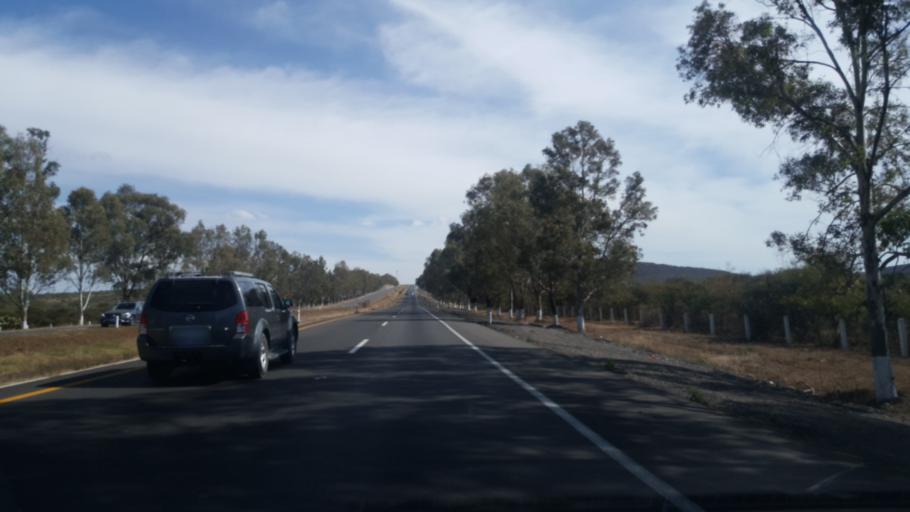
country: MX
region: Jalisco
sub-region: Lagos de Moreno
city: Cristeros [Fraccionamiento]
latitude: 21.2706
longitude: -101.9737
